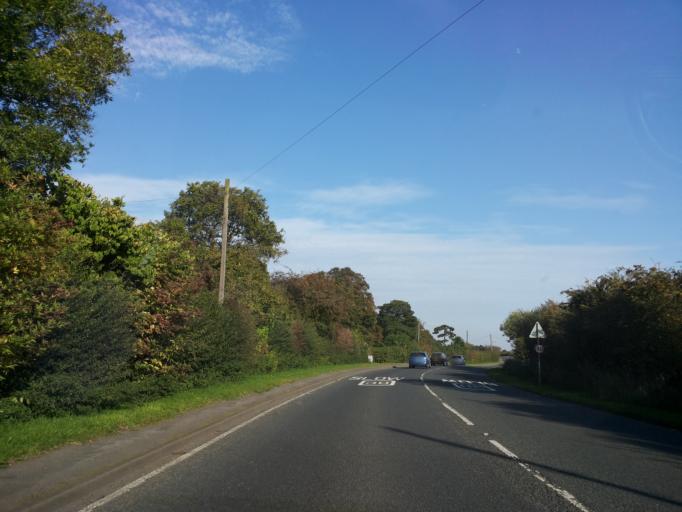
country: GB
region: England
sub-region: East Riding of Yorkshire
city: Snaith
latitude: 53.6851
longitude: -0.9930
